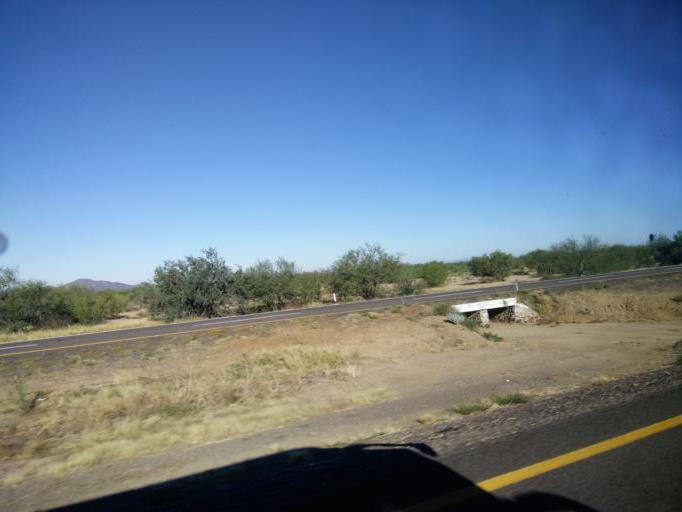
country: MX
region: Sonora
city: Hermosillo
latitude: 28.7715
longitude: -110.9668
